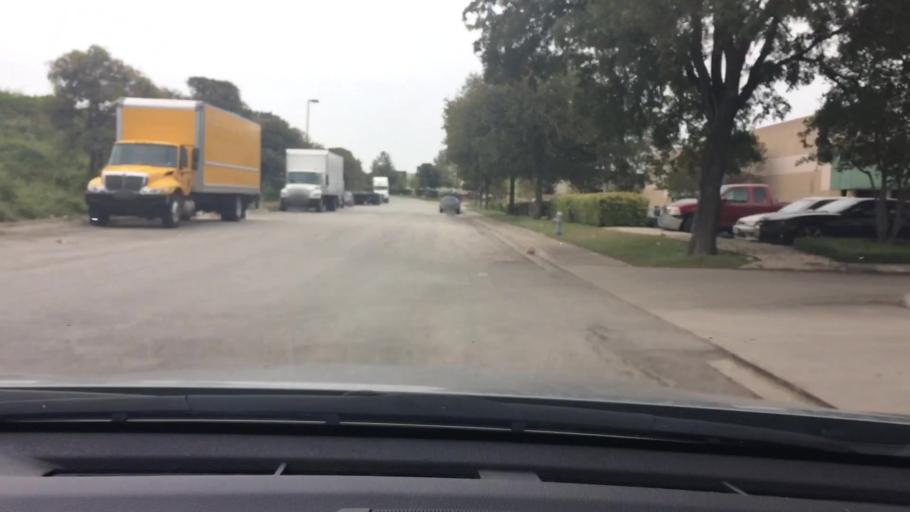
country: US
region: Texas
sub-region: Bexar County
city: Windcrest
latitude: 29.5414
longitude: -98.3722
